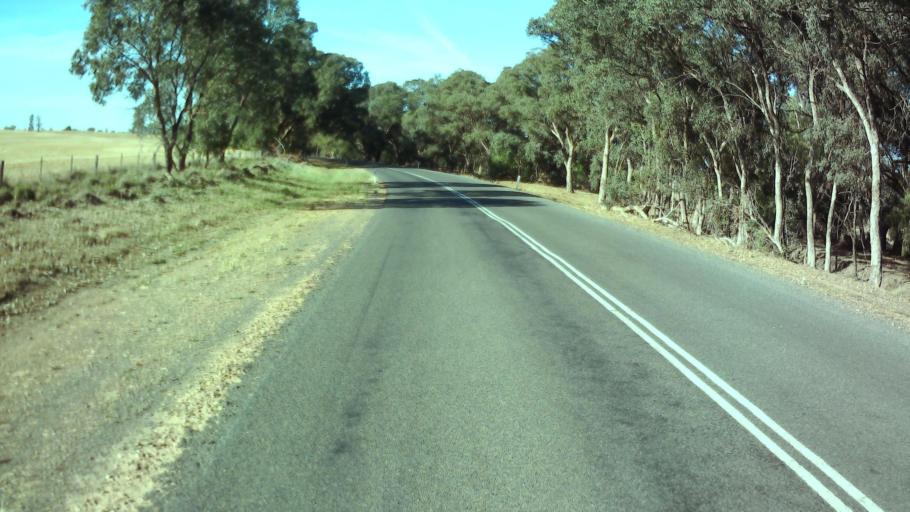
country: AU
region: New South Wales
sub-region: Weddin
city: Grenfell
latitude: -33.9940
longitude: 148.1332
